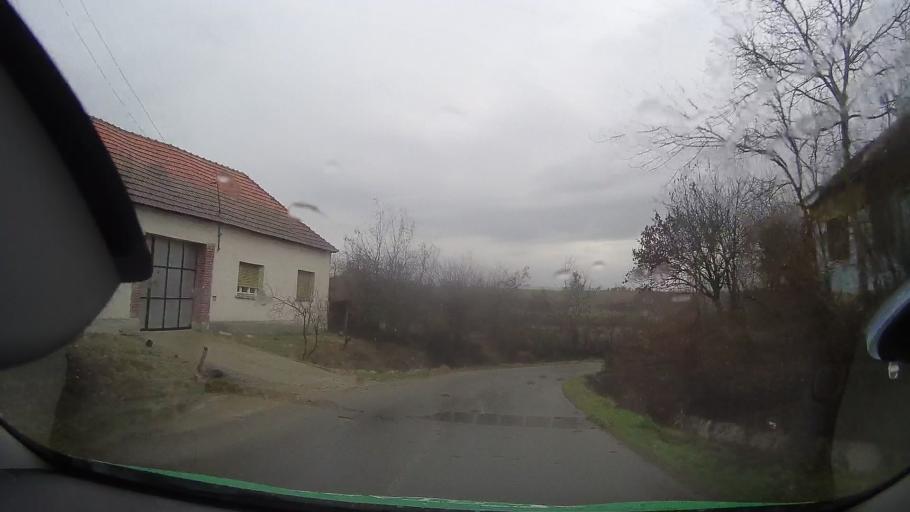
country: RO
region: Bihor
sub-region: Comuna Holod
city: Vintere
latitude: 46.7449
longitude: 22.1376
